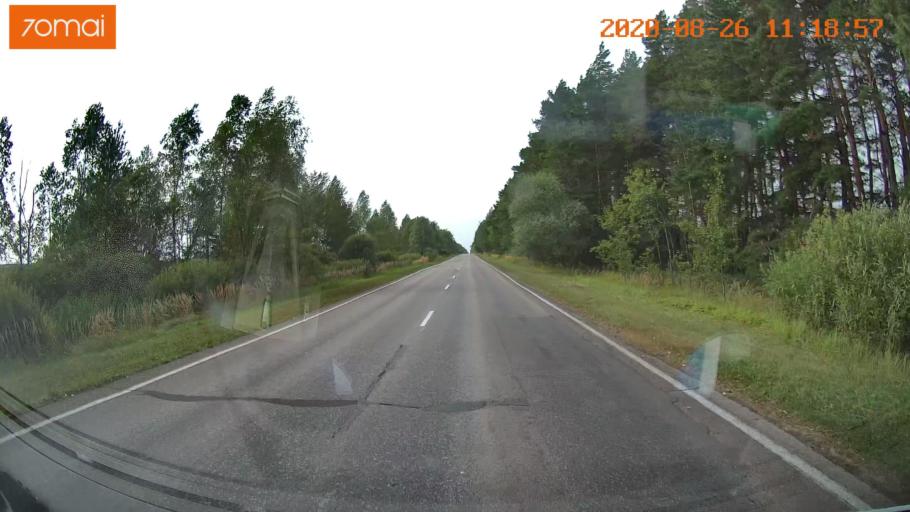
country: RU
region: Rjazan
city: Shilovo
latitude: 54.4046
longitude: 41.0881
